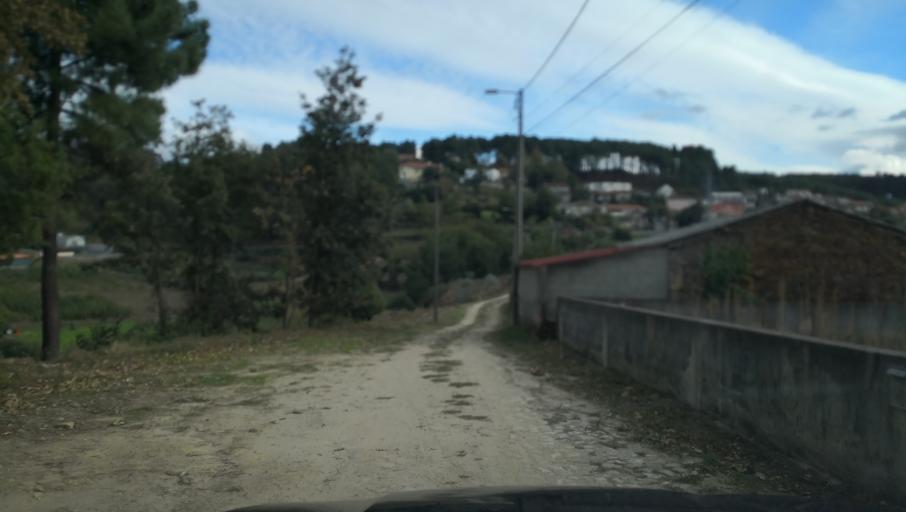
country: PT
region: Vila Real
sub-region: Vila Real
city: Vila Real
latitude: 41.2894
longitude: -7.7090
